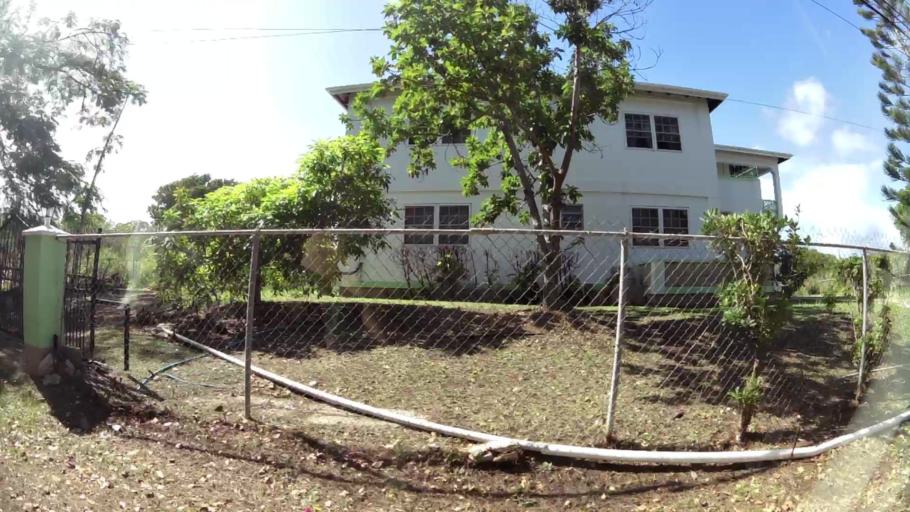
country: AG
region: Saint George
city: Piggotts
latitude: 17.1675
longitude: -61.8020
